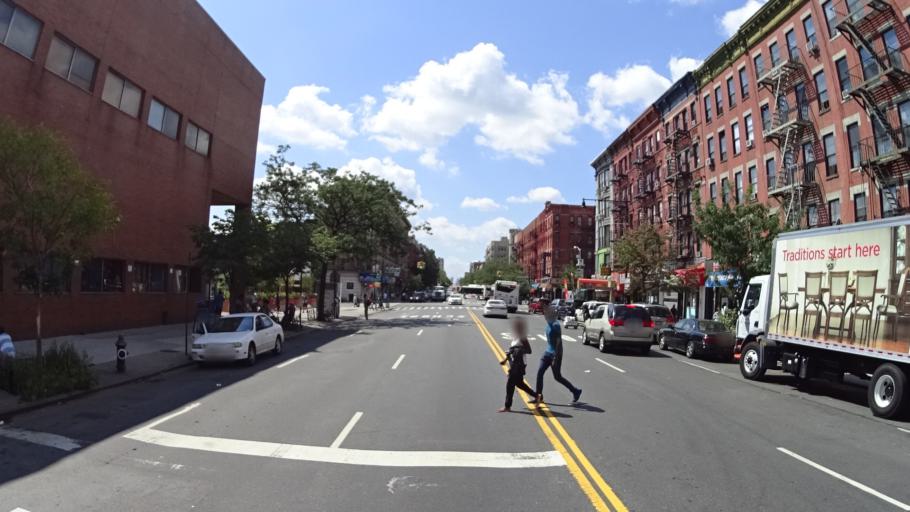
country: US
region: New Jersey
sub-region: Bergen County
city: Edgewater
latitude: 40.8258
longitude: -73.9472
